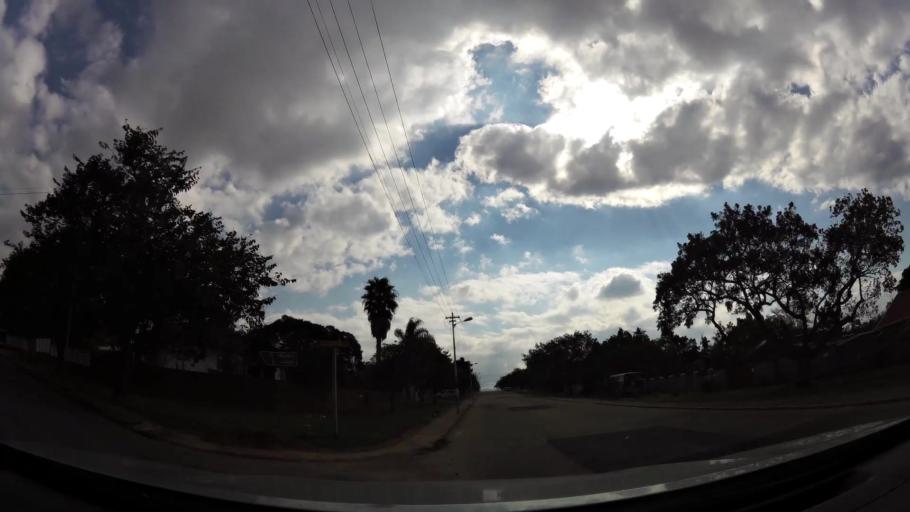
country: ZA
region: Eastern Cape
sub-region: Nelson Mandela Bay Metropolitan Municipality
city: Uitenhage
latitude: -33.7515
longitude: 25.4090
